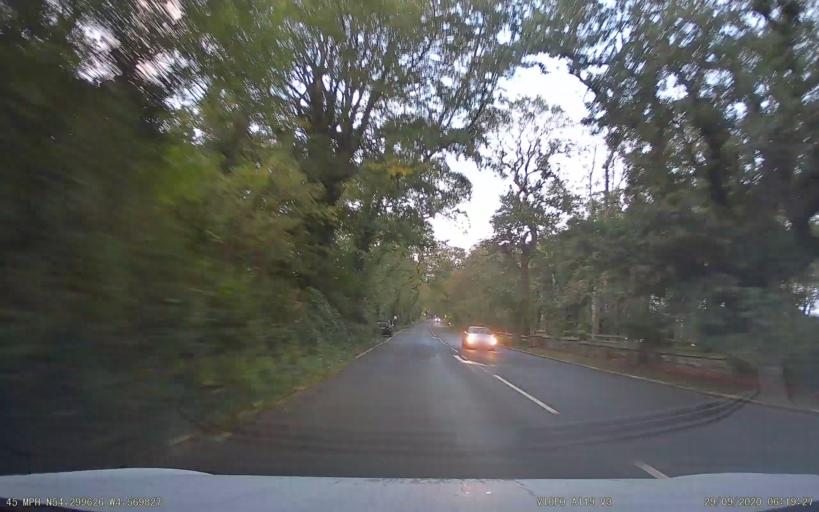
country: IM
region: Douglas
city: Douglas
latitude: 54.2996
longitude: -4.5698
